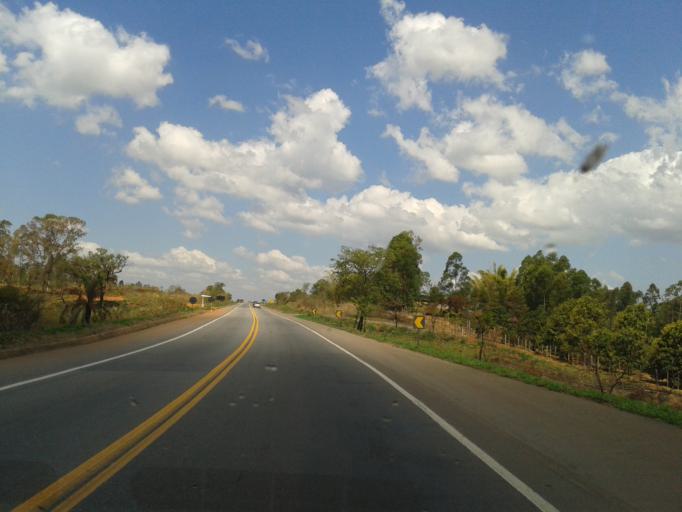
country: BR
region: Minas Gerais
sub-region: Campos Altos
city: Campos Altos
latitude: -19.6811
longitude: -46.0426
